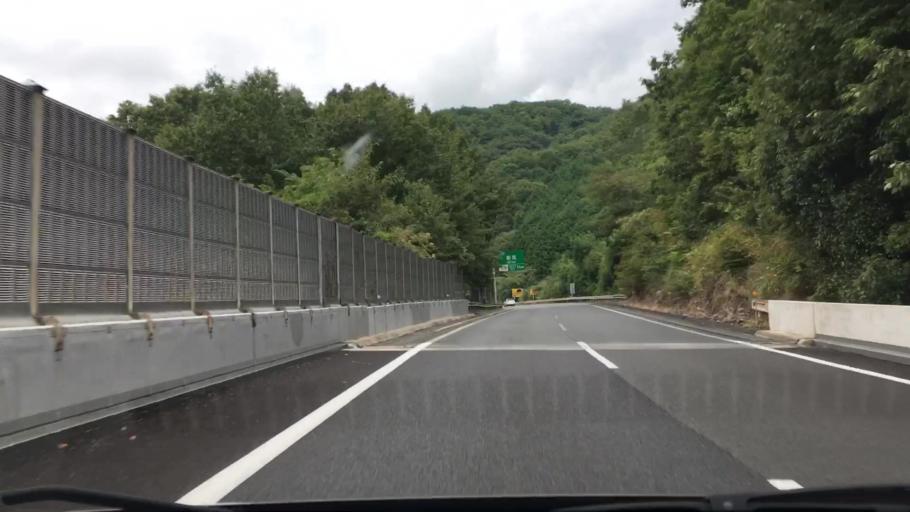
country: JP
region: Okayama
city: Niimi
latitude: 34.9910
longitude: 133.4598
